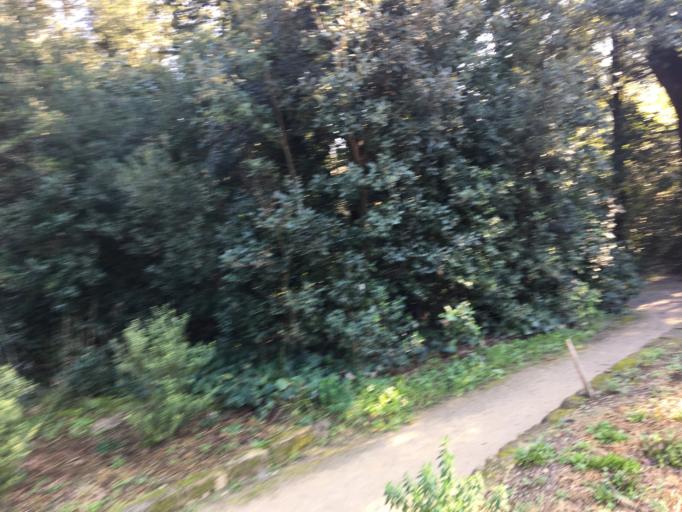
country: FR
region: Languedoc-Roussillon
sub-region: Departement de l'Herault
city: Montpellier
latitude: 43.6141
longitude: 3.8712
